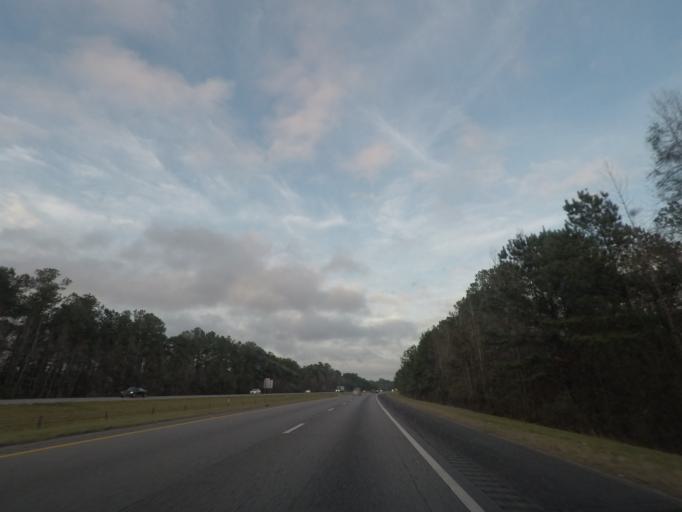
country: US
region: South Carolina
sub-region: Orangeburg County
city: Holly Hill
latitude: 33.3993
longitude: -80.5115
